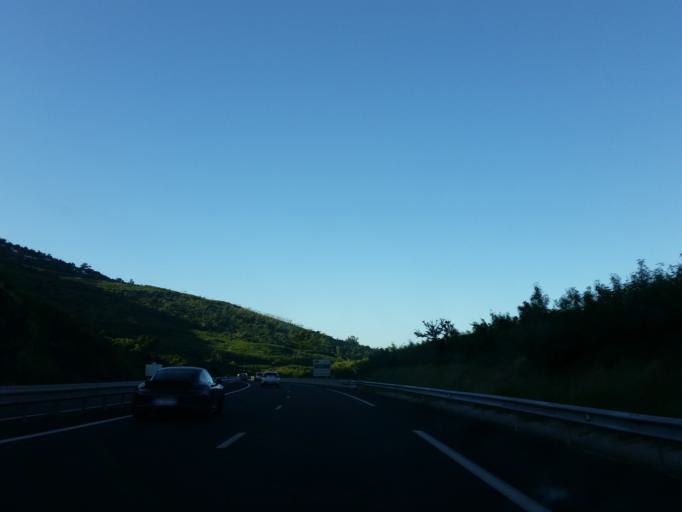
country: RE
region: Reunion
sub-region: Reunion
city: Trois-Bassins
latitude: -21.1307
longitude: 55.2830
